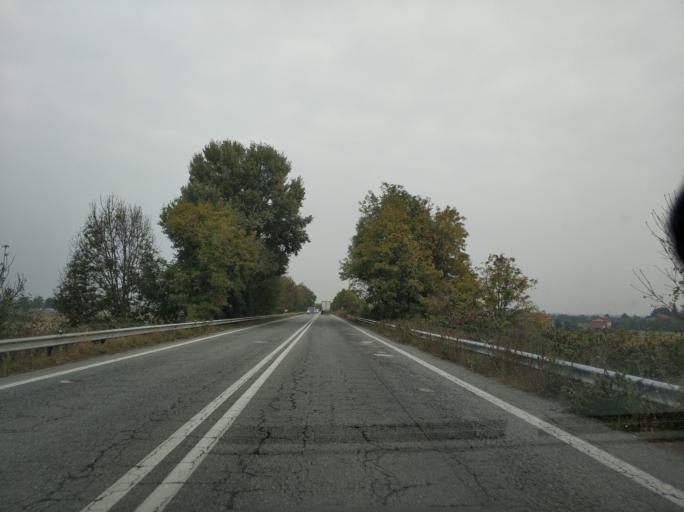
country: IT
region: Piedmont
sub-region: Provincia di Torino
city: Leini
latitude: 45.1863
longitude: 7.6931
